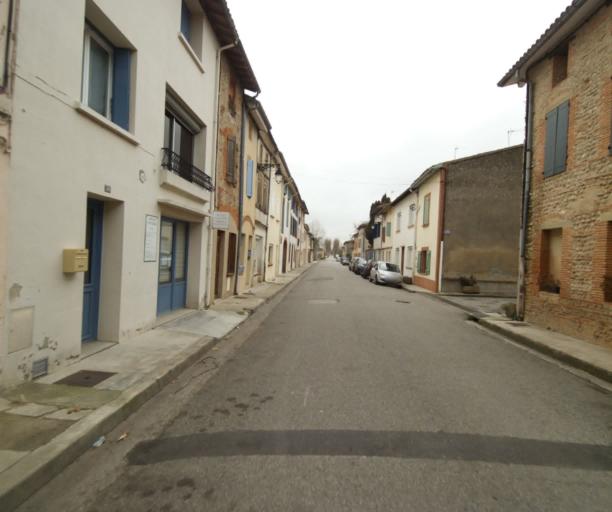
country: FR
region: Midi-Pyrenees
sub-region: Departement de l'Ariege
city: Mazeres
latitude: 43.2504
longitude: 1.6798
